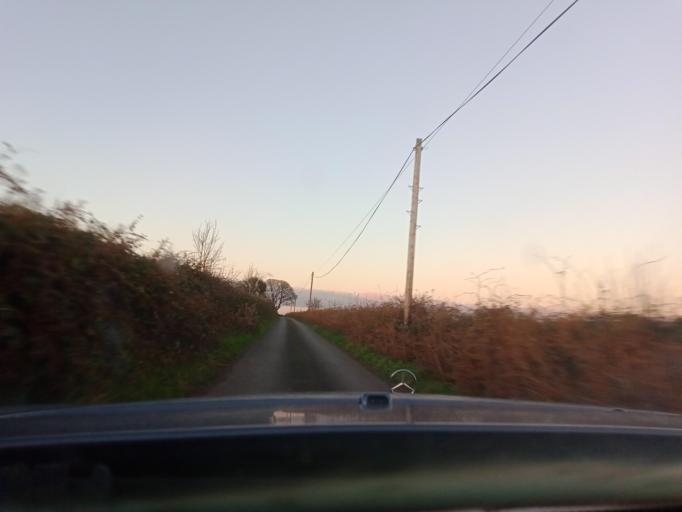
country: IE
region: Leinster
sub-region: Kilkenny
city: Graiguenamanagh
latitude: 52.5576
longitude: -6.9628
